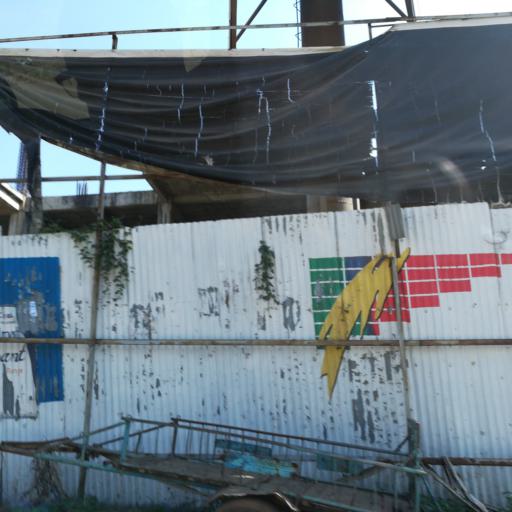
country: KE
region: Nairobi Area
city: Nairobi
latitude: -1.2987
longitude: 36.7973
